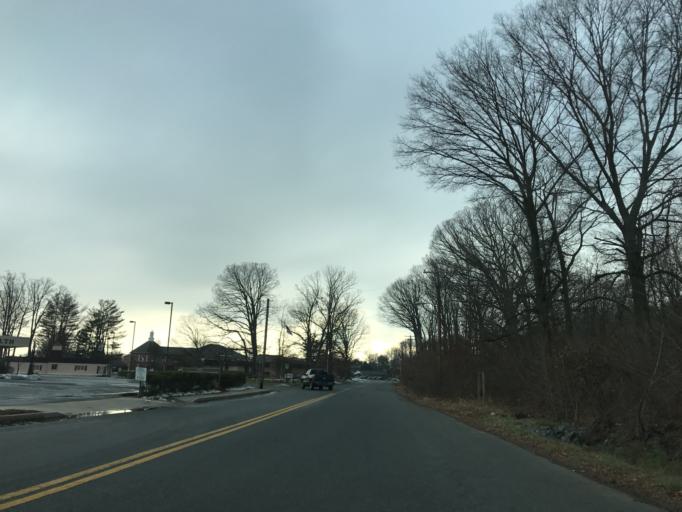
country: US
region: Maryland
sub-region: Harford County
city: Aberdeen
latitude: 39.5139
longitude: -76.1626
